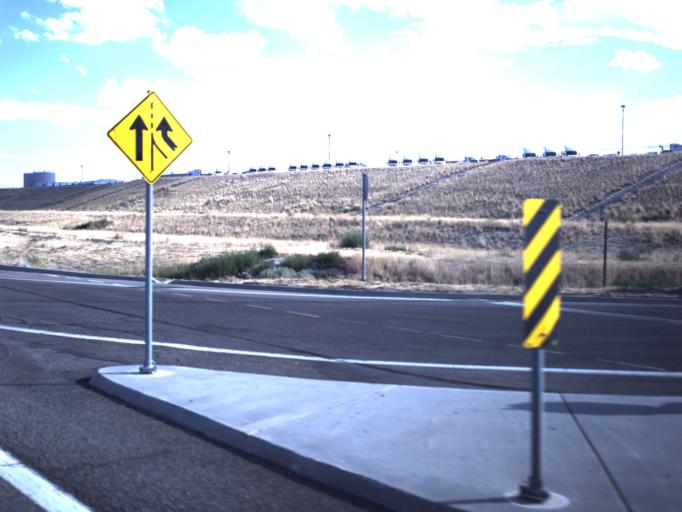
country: US
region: Utah
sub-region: Tooele County
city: Grantsville
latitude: 40.6257
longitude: -112.5084
